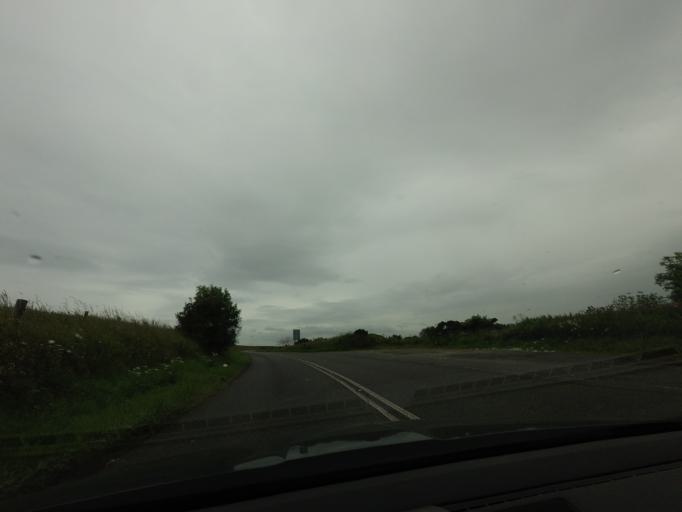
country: GB
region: Scotland
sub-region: Aberdeenshire
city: Portsoy
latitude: 57.6738
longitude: -2.6865
